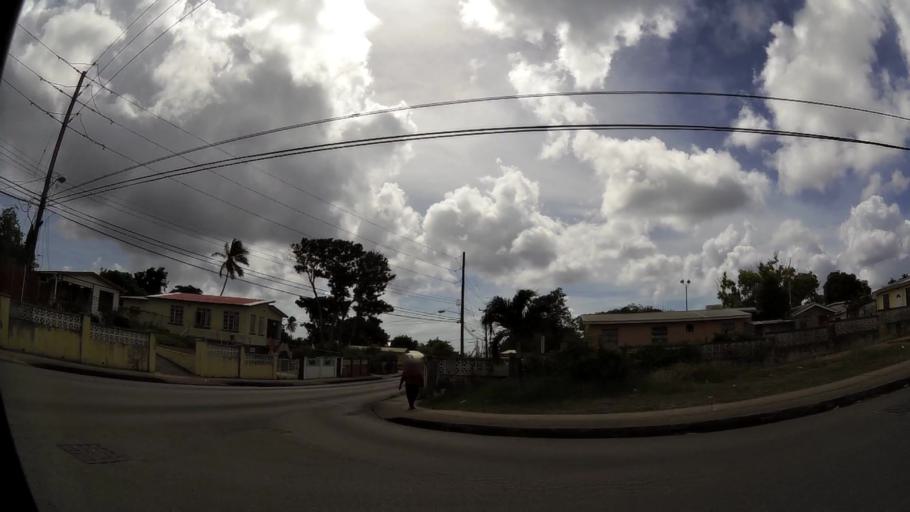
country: BB
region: Saint Michael
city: Bridgetown
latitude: 13.1238
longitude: -59.6081
